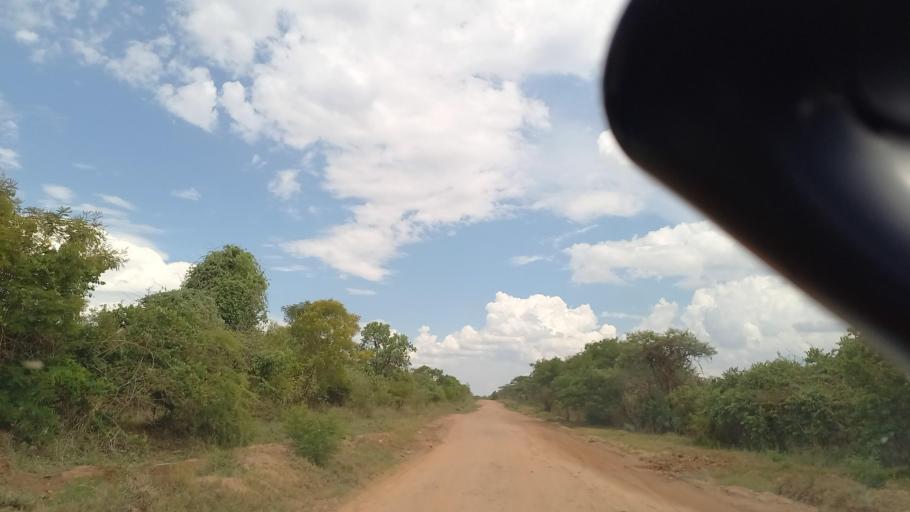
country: ZM
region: Southern
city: Nakambala
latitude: -16.0482
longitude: 27.9797
